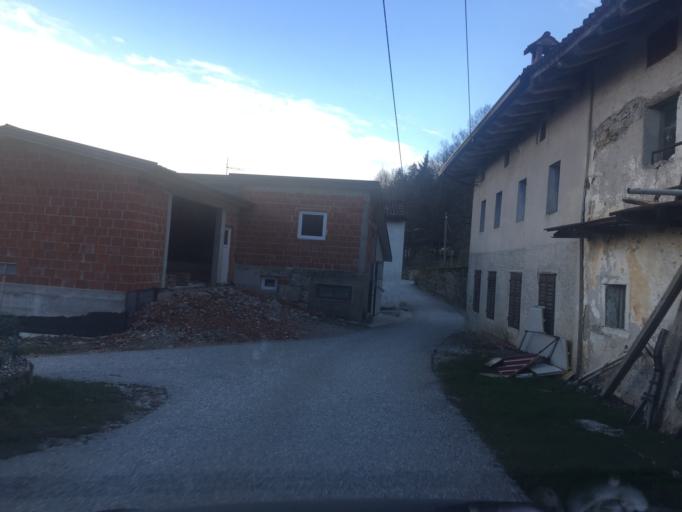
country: SI
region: Kanal
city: Deskle
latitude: 46.0393
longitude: 13.6622
